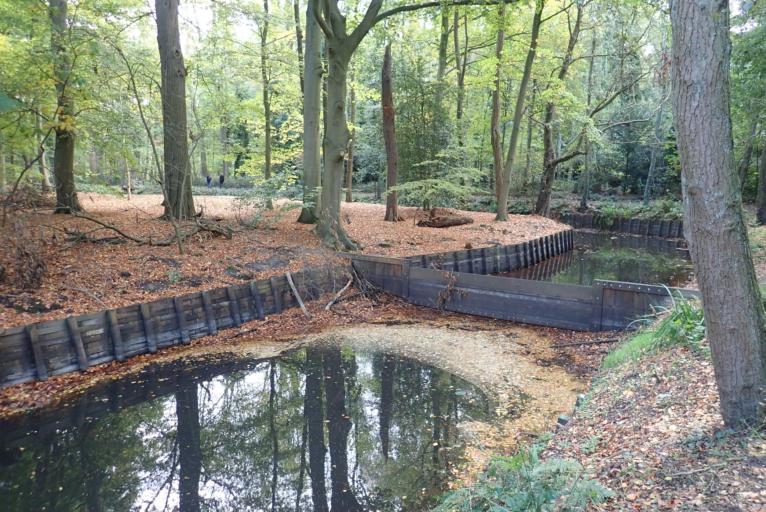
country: BE
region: Flanders
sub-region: Provincie Antwerpen
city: Rumst
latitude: 51.0710
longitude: 4.4635
